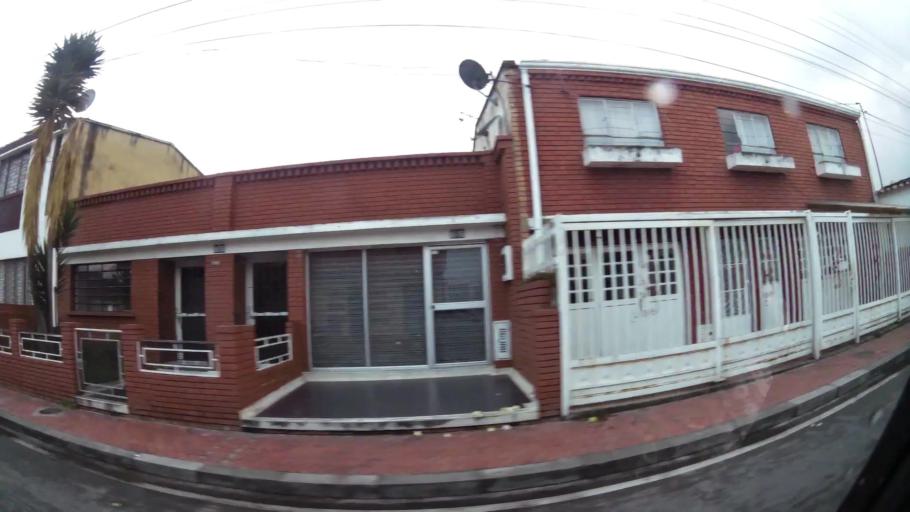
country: CO
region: Cundinamarca
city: Chia
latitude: 4.8607
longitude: -74.0579
